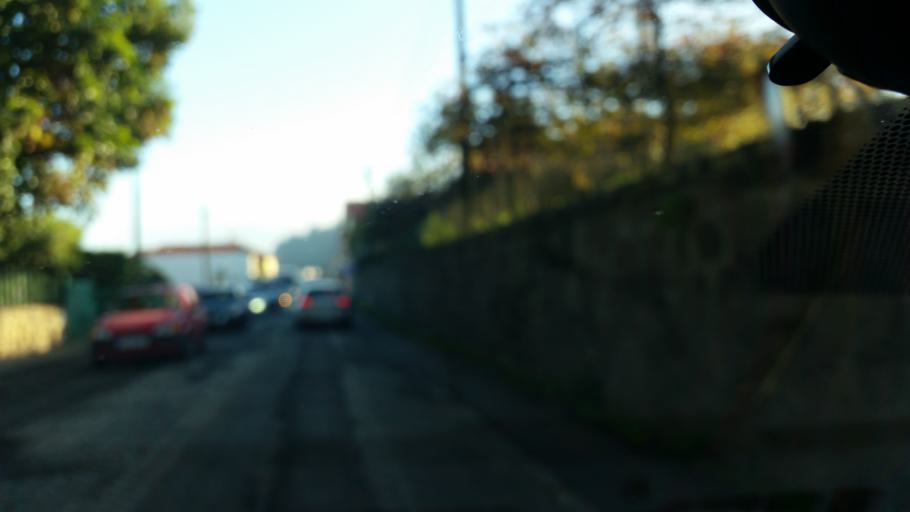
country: PT
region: Porto
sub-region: Santo Tirso
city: Sao Miguel do Couto
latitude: 41.3501
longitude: -8.4540
